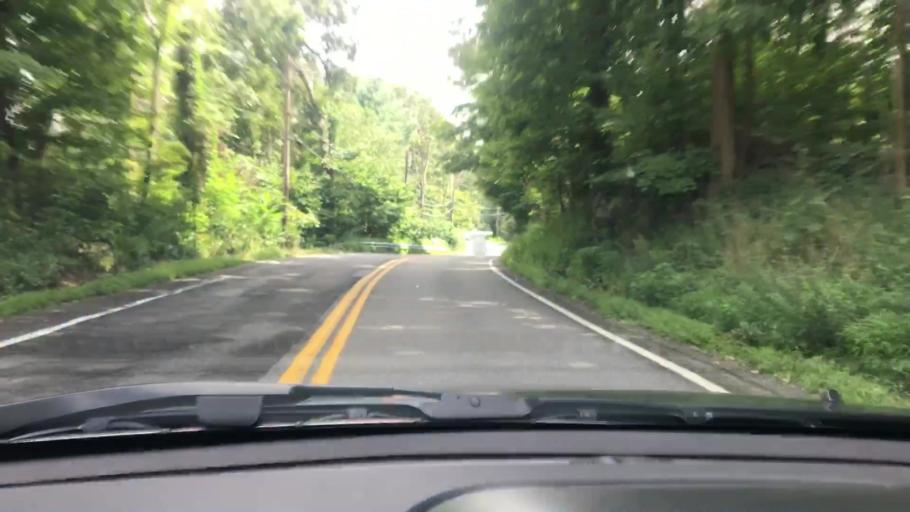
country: US
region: New York
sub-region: Westchester County
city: Pound Ridge
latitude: 41.1638
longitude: -73.5995
